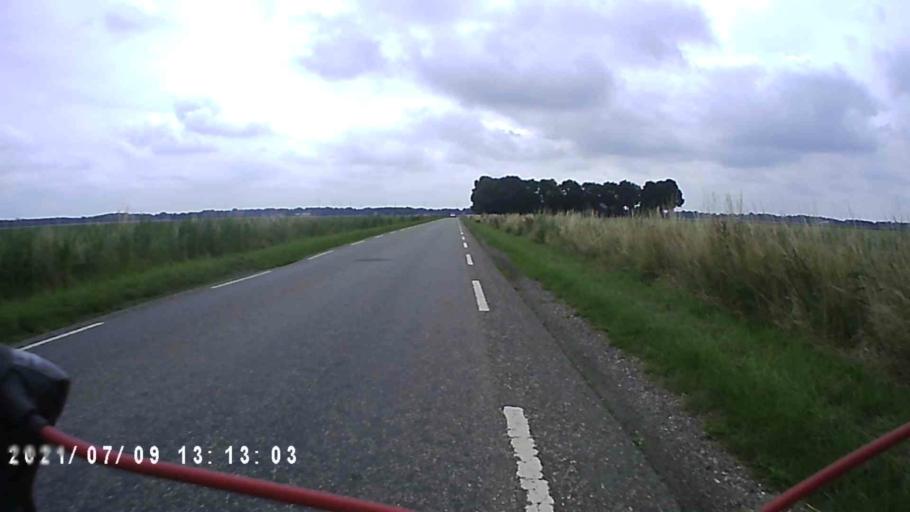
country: NL
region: Groningen
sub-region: Gemeente Vlagtwedde
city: Vlagtwedde
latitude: 53.1228
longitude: 7.1402
